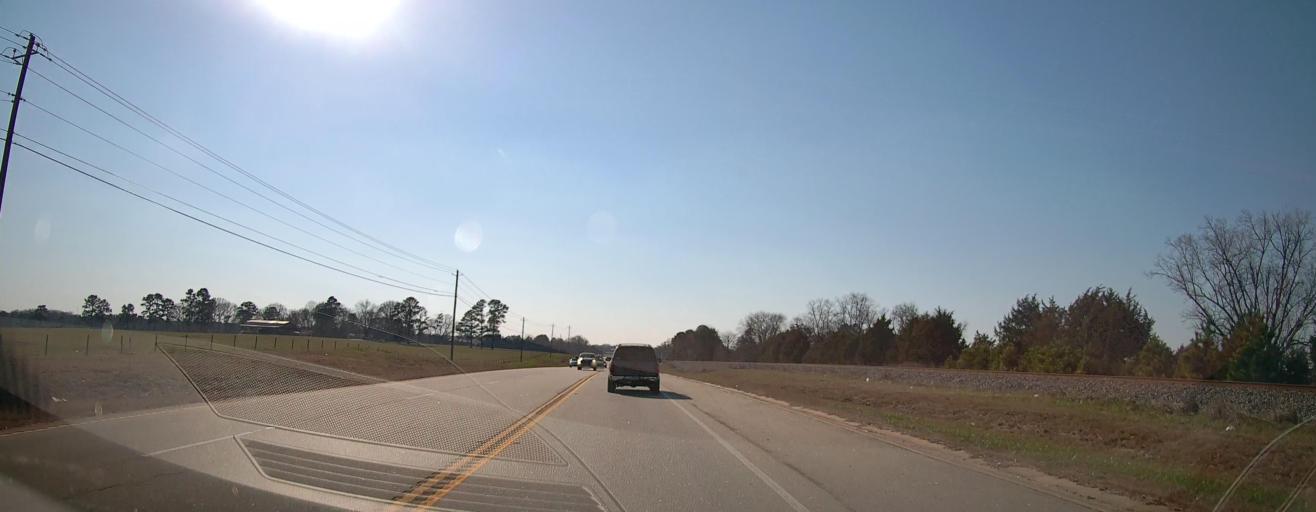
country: US
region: Georgia
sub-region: Butts County
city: Jackson
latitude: 33.3264
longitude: -84.0087
